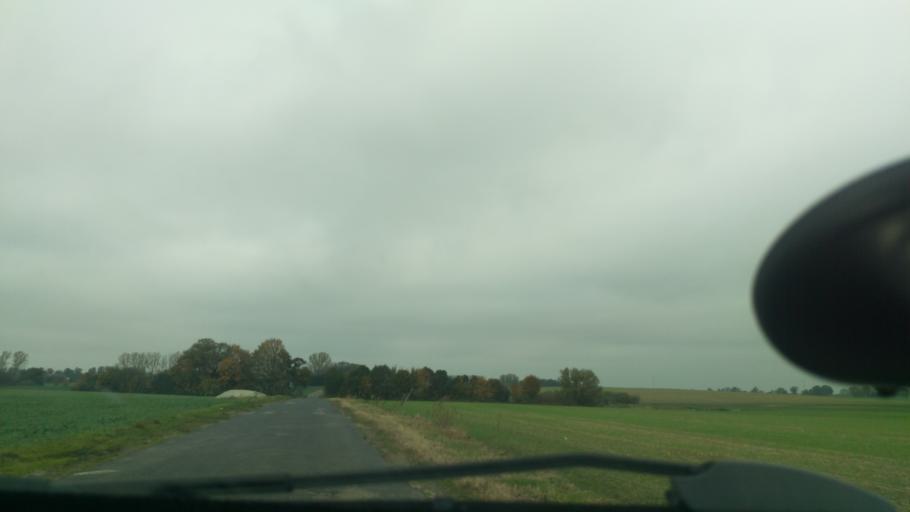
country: PL
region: West Pomeranian Voivodeship
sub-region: Powiat pyrzycki
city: Przelewice
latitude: 53.0681
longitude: 15.1030
